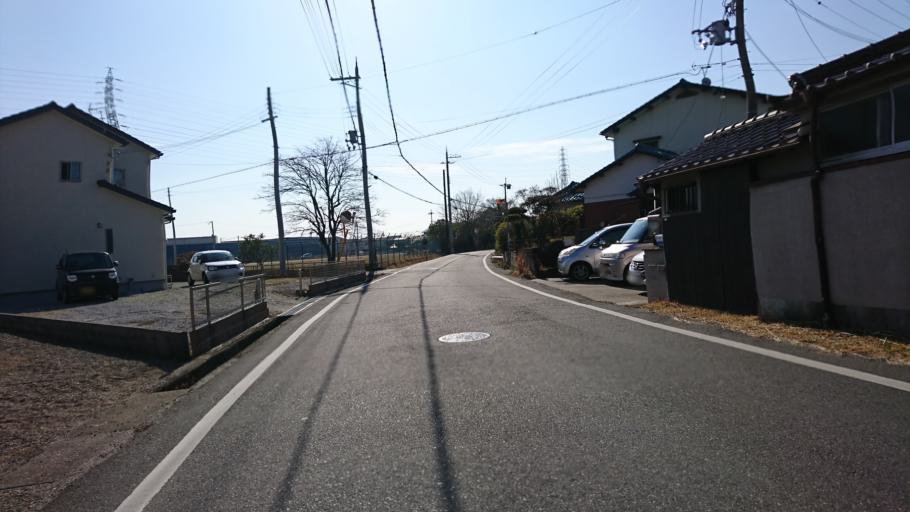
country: JP
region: Hyogo
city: Kakogawacho-honmachi
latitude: 34.7901
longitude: 134.8312
